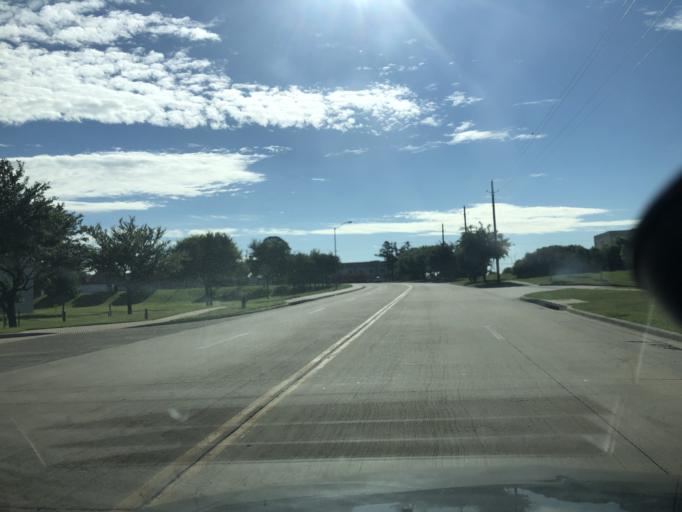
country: US
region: Texas
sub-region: Tarrant County
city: Euless
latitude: 32.8075
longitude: -97.0324
